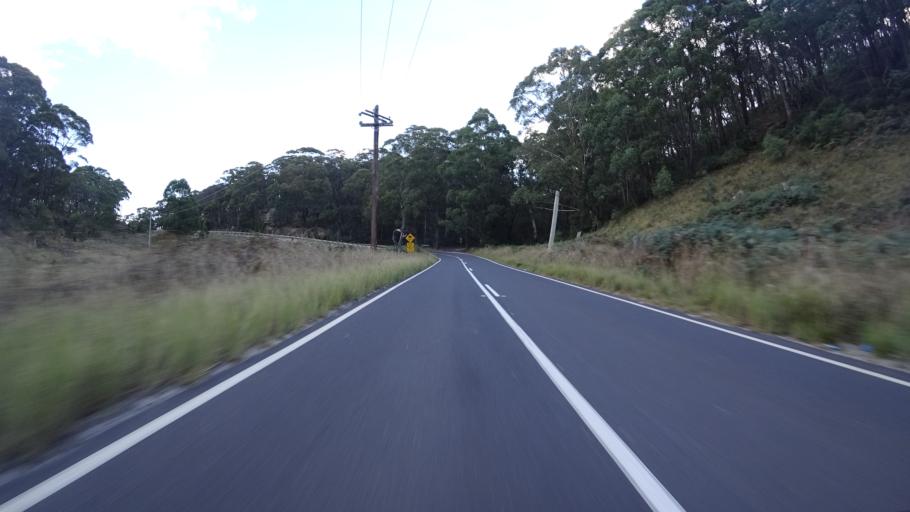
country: AU
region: New South Wales
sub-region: Lithgow
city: Lithgow
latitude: -33.4992
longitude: 150.1714
